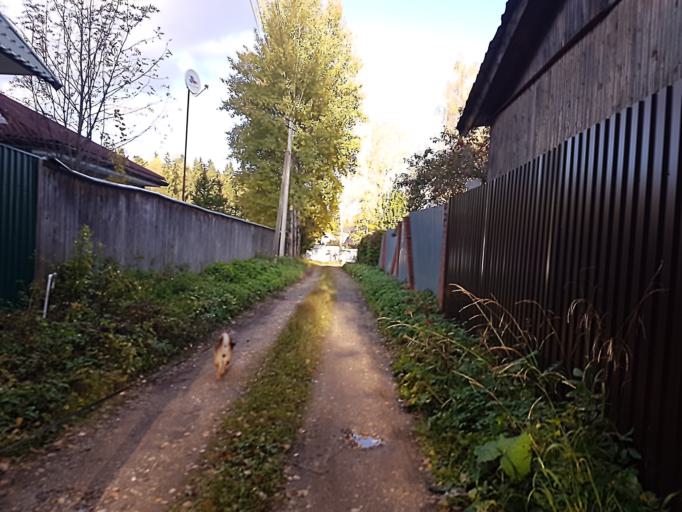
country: RU
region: Moskovskaya
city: Istra
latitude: 55.9194
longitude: 36.8846
